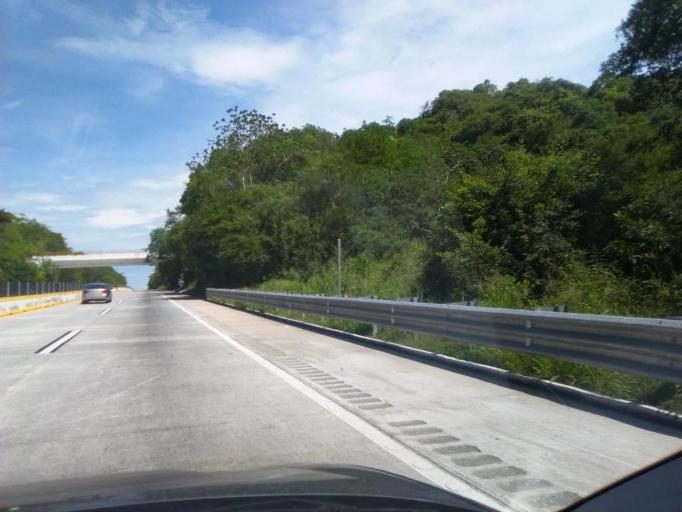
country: MX
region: Guerrero
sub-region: Acapulco de Juarez
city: Kilometro 30
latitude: 16.9795
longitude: -99.7160
